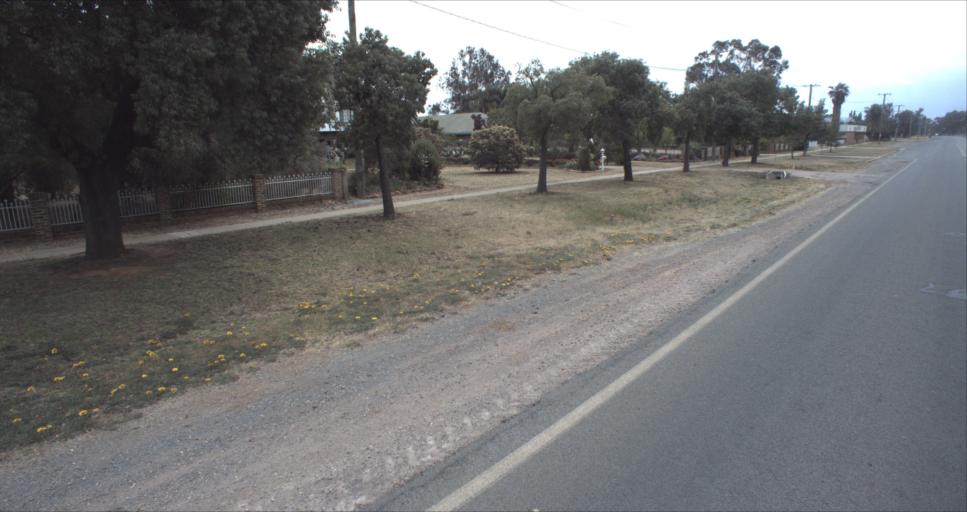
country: AU
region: New South Wales
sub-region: Leeton
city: Leeton
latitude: -34.5385
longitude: 146.4077
